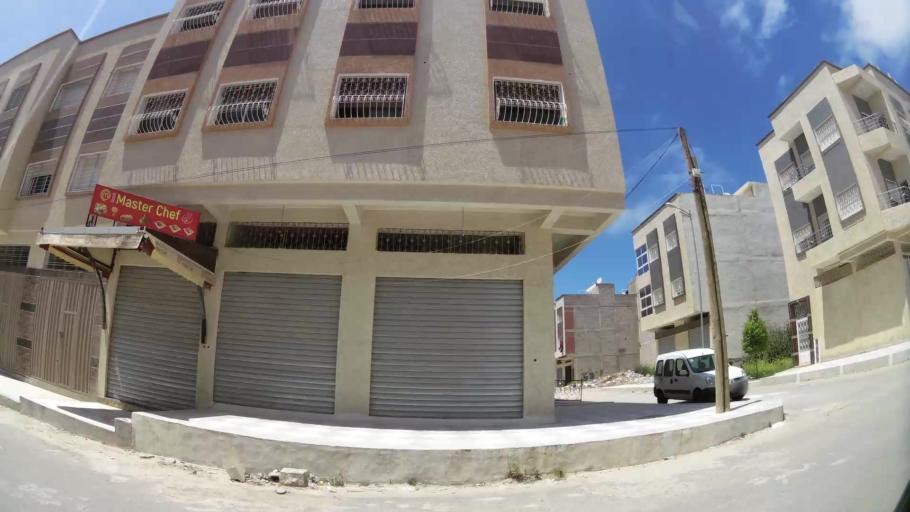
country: MA
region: Fes-Boulemane
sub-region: Fes
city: Fes
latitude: 34.0549
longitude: -5.0378
